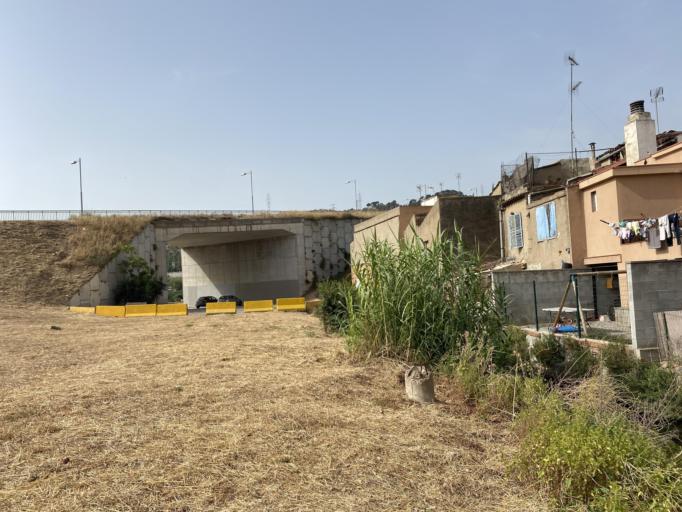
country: ES
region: Catalonia
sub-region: Provincia de Barcelona
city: Montcada i Reixac
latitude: 41.4622
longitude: 2.1843
